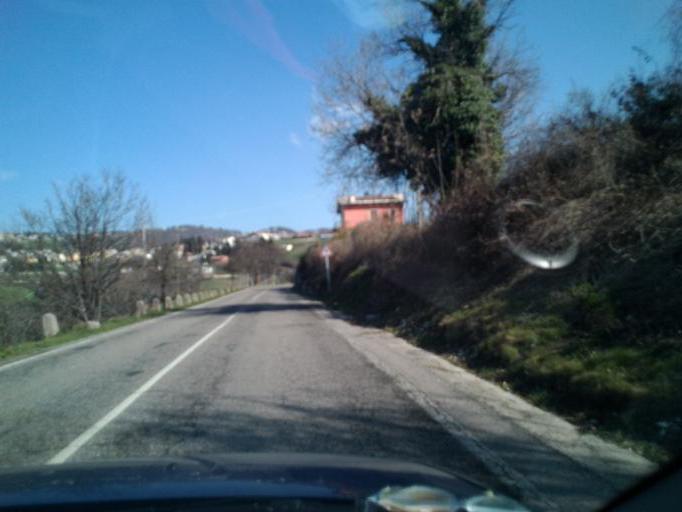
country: IT
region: Veneto
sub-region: Provincia di Verona
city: Cerro Veronese
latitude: 45.5919
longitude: 11.0343
